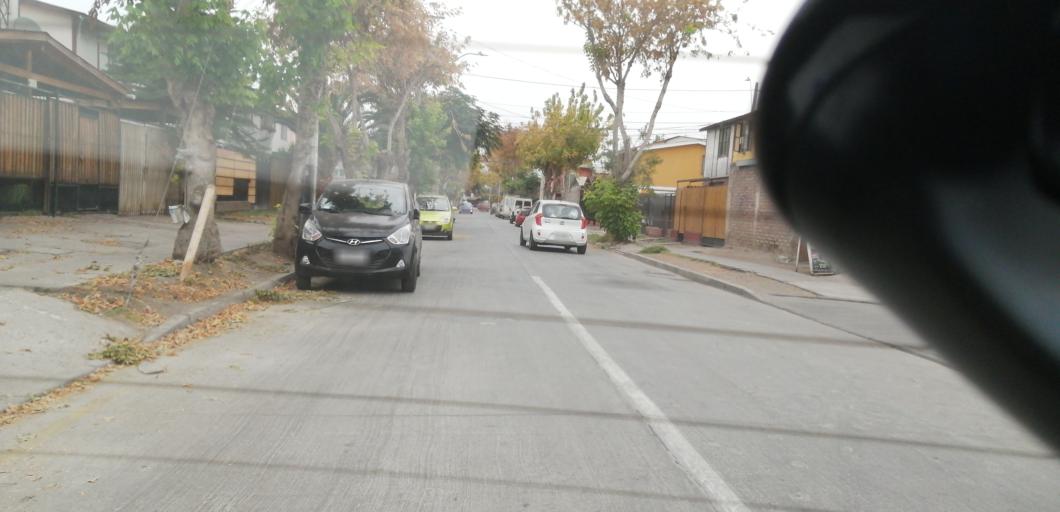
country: CL
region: Santiago Metropolitan
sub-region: Provincia de Santiago
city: Lo Prado
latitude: -33.4555
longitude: -70.7625
